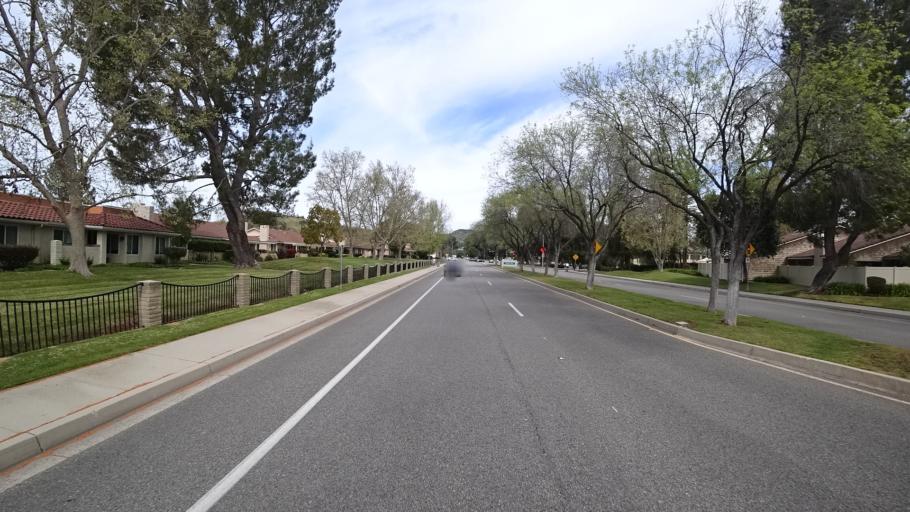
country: US
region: California
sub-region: Ventura County
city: Thousand Oaks
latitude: 34.1479
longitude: -118.8379
